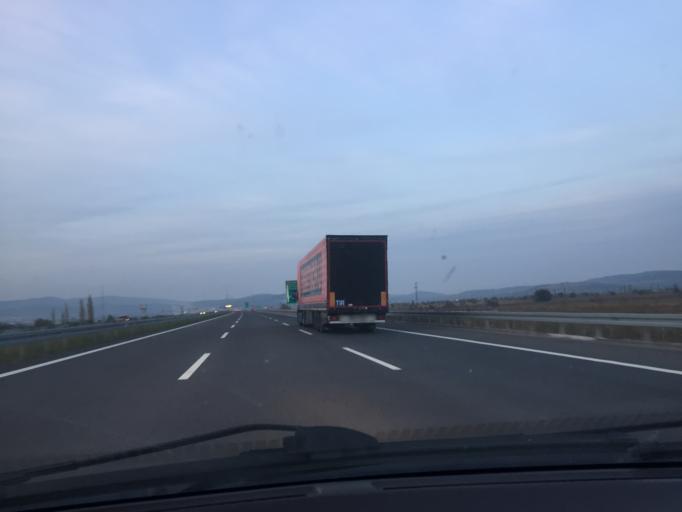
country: TR
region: Manisa
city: Halitpasa
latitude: 38.7536
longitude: 27.6601
